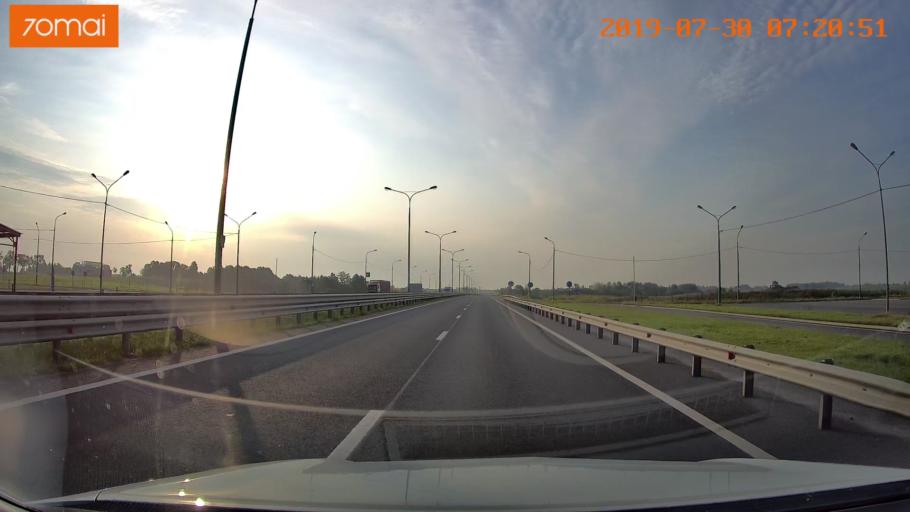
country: RU
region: Kaliningrad
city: Bol'shoe Isakovo
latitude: 54.6991
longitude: 20.7134
